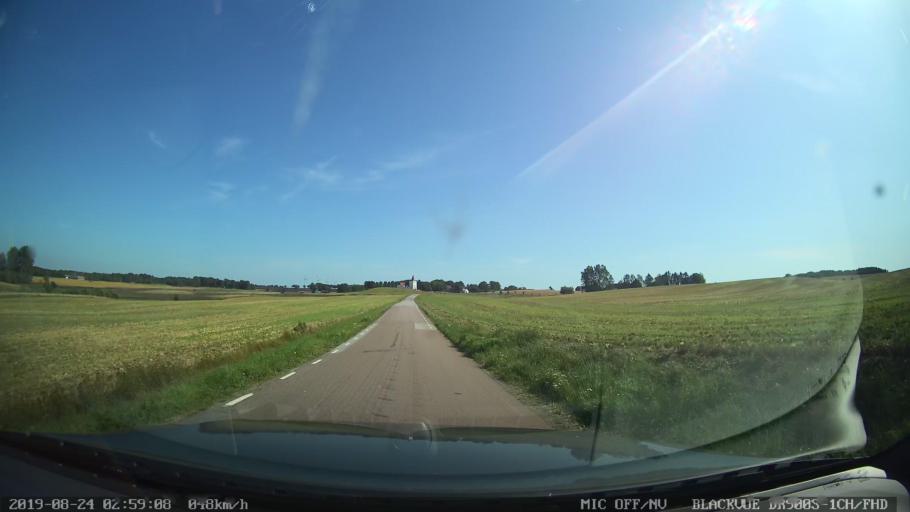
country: SE
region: Skane
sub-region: Skurups Kommun
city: Skurup
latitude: 55.4686
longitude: 13.4234
